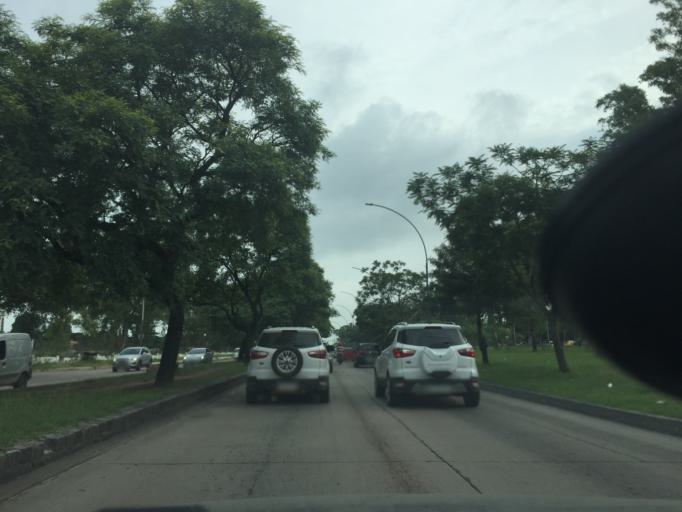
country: AR
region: Cordoba
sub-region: Departamento de Capital
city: Cordoba
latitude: -31.4386
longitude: -64.1962
